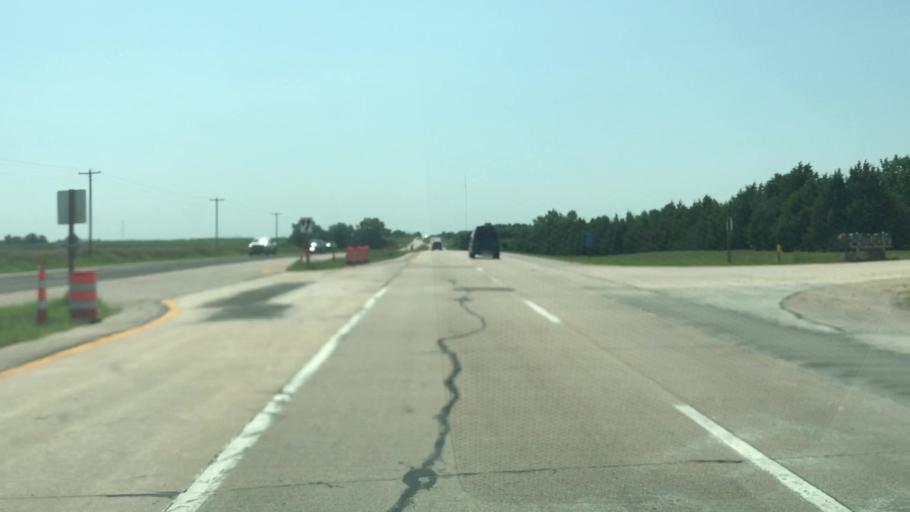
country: US
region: Nebraska
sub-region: Adams County
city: Hastings
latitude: 40.6772
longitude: -98.3822
